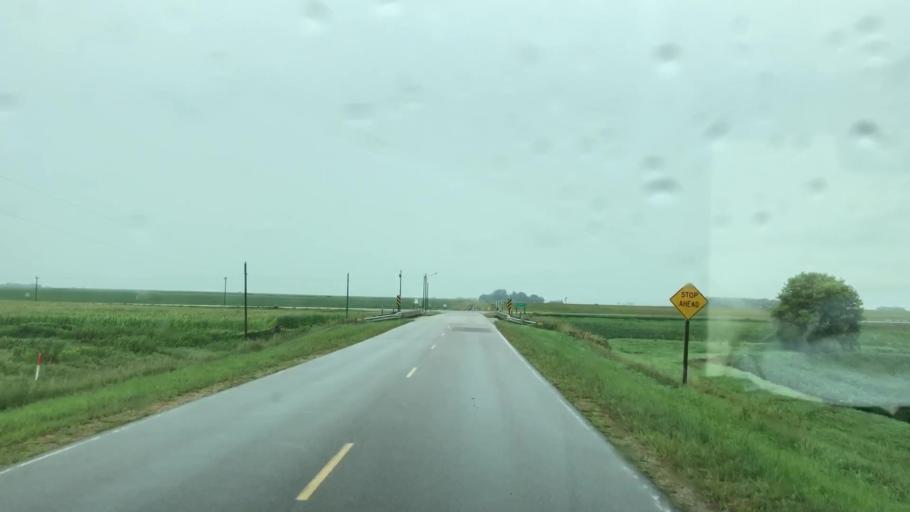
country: US
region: Iowa
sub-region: O'Brien County
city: Sanborn
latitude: 43.1882
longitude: -95.7230
